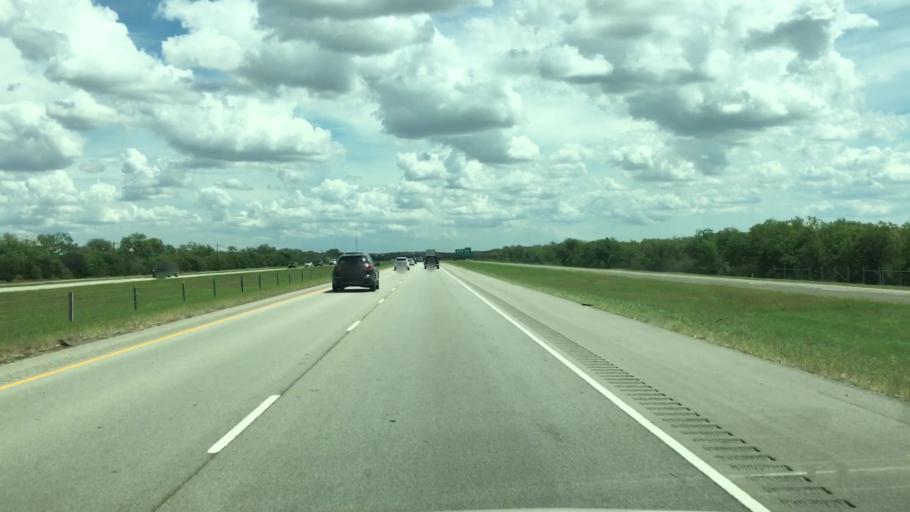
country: US
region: Texas
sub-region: Live Oak County
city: George West
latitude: 28.2771
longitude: -97.9517
